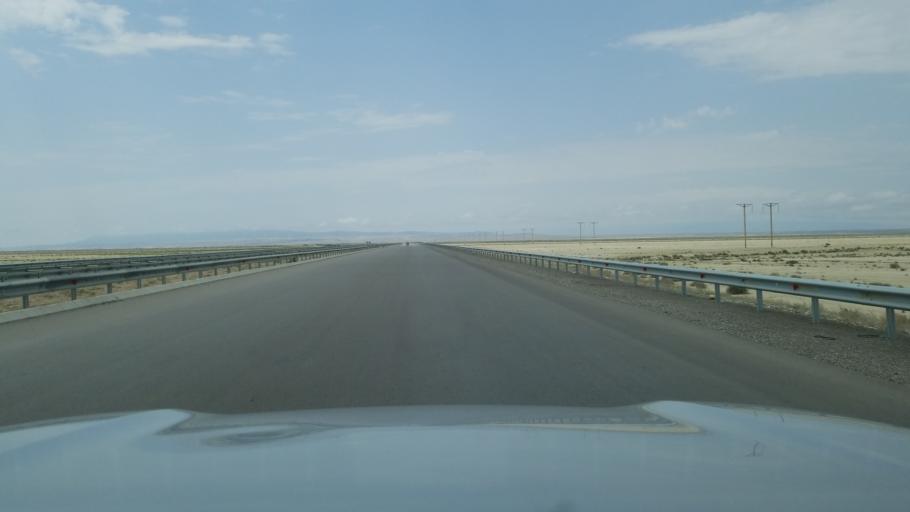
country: TM
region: Balkan
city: Gazanjyk
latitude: 39.2674
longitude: 55.2931
